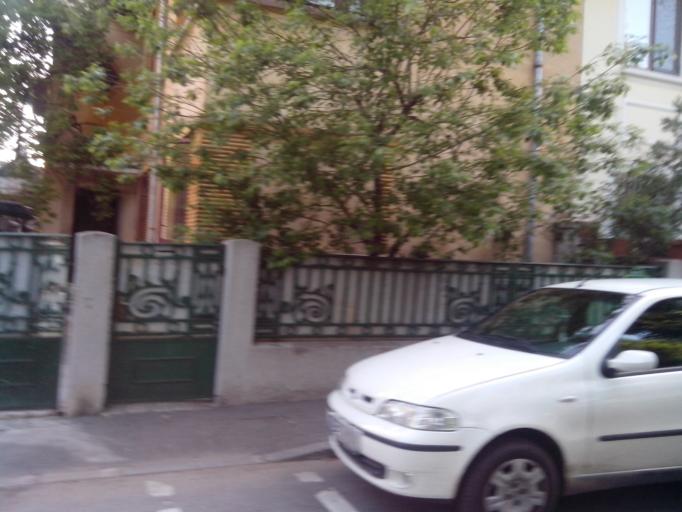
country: RO
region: Ilfov
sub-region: Comuna Fundeni-Dobroesti
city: Fundeni
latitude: 44.4408
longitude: 26.1421
